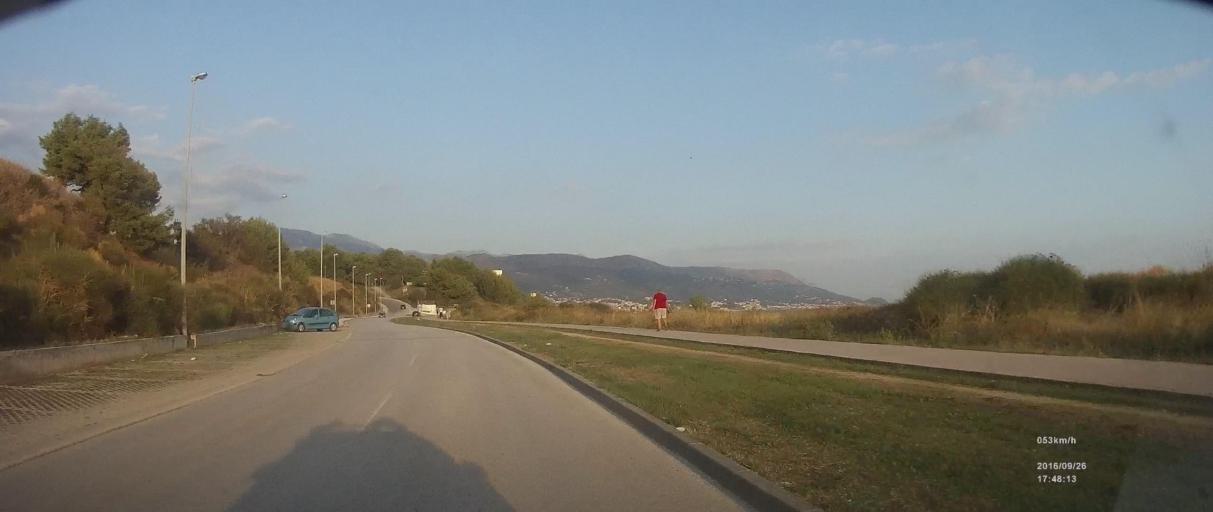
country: HR
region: Splitsko-Dalmatinska
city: Kamen
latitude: 43.5017
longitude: 16.4895
